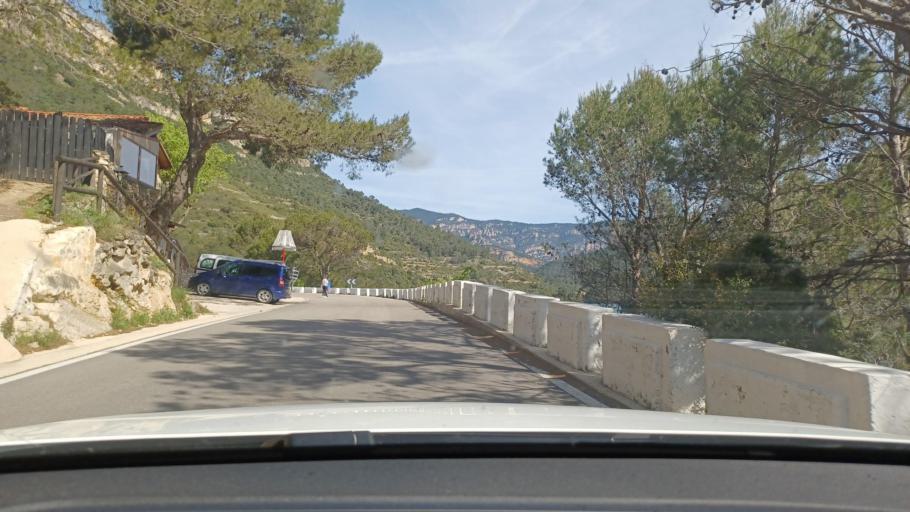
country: ES
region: Valencia
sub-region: Provincia de Castello
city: Rosell
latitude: 40.6708
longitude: 0.2331
